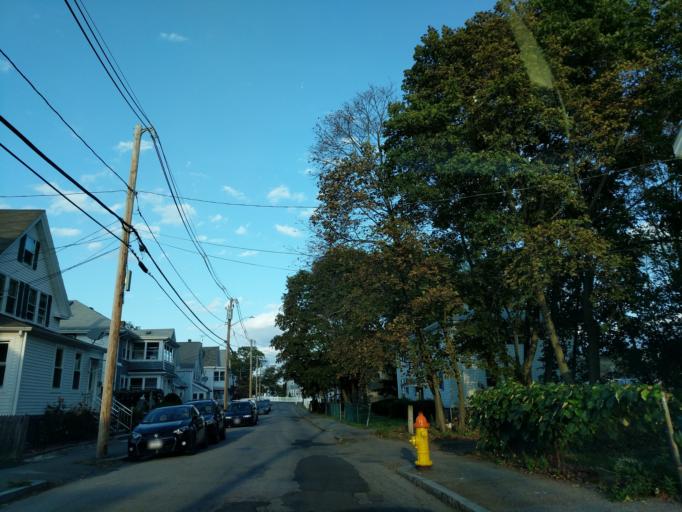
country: US
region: Massachusetts
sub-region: Norfolk County
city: Quincy
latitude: 42.2795
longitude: -71.0300
